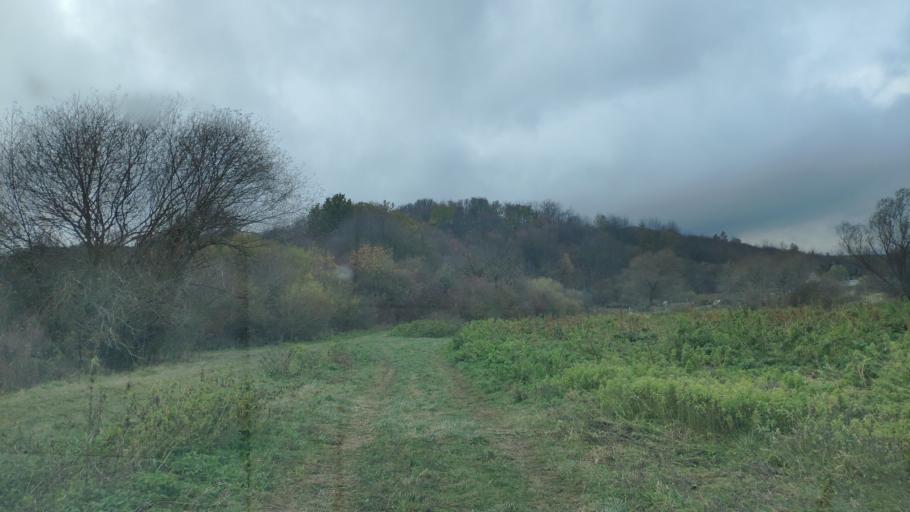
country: SK
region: Presovsky
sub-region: Okres Presov
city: Presov
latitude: 49.0133
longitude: 21.2002
